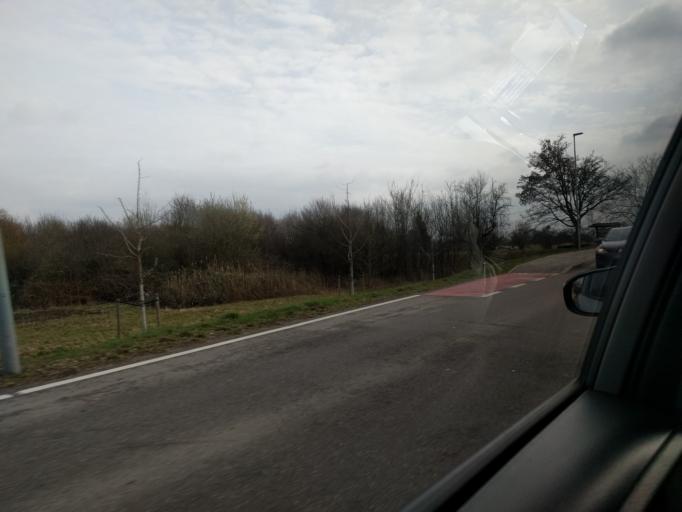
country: DE
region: Rheinland-Pfalz
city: Neuburg
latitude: 48.9684
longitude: 8.2700
